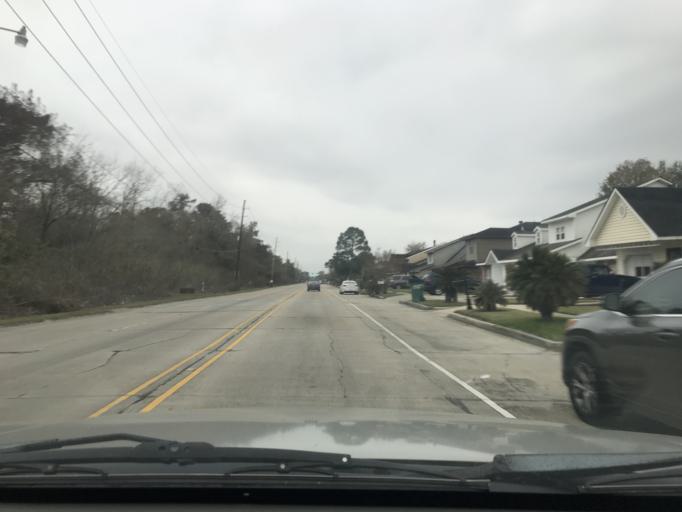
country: US
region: Louisiana
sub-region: Jefferson Parish
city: Woodmere
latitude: 29.8612
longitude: -90.0727
